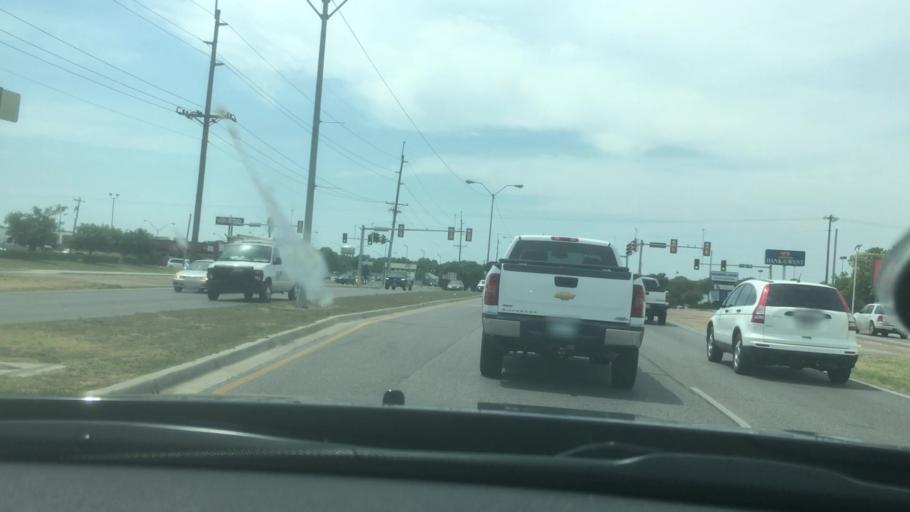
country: US
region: Oklahoma
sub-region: Carter County
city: Ardmore
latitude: 34.1812
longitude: -97.1431
